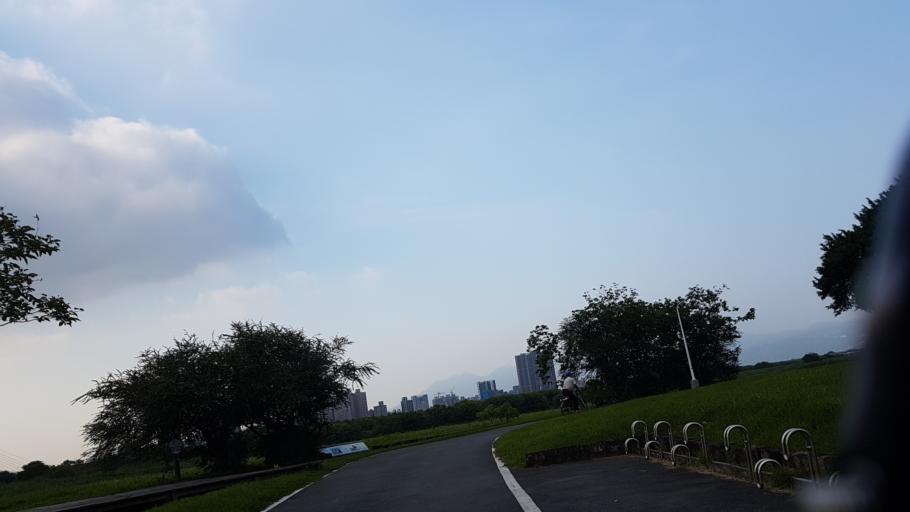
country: TW
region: Taipei
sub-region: Taipei
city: Banqiao
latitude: 25.0374
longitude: 121.4905
